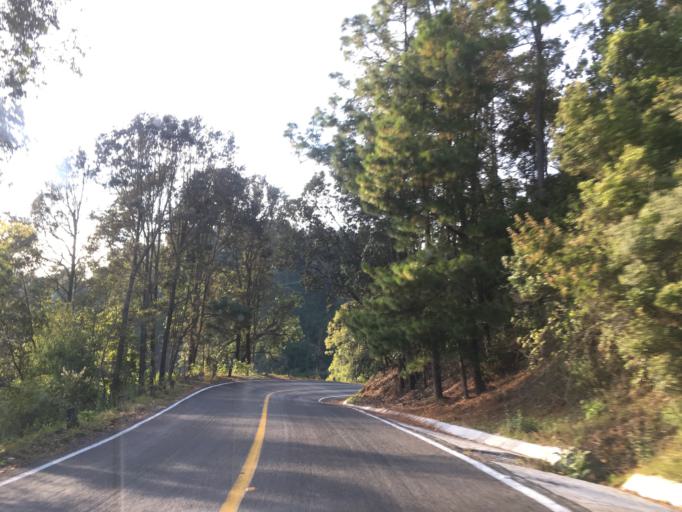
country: MX
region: Michoacan
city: Tzitzio
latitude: 19.6677
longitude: -100.9068
